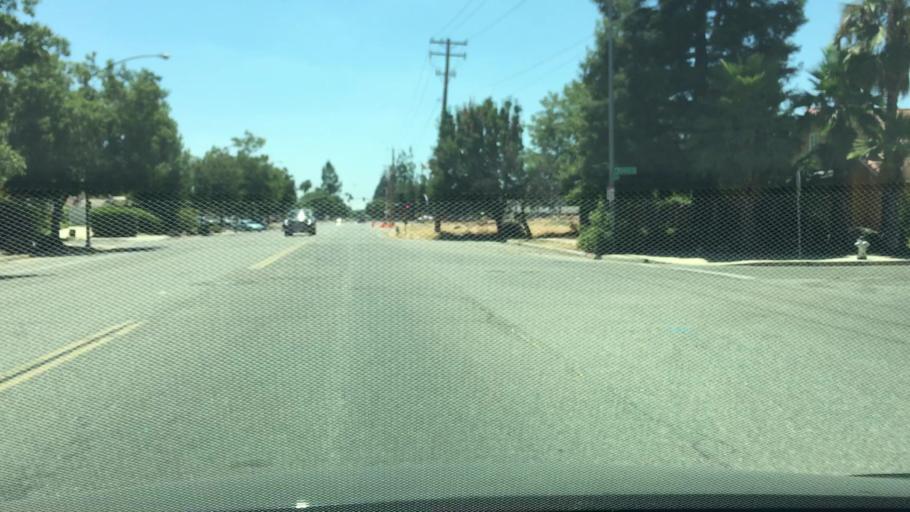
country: US
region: California
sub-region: Fresno County
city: Clovis
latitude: 36.8544
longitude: -119.7478
